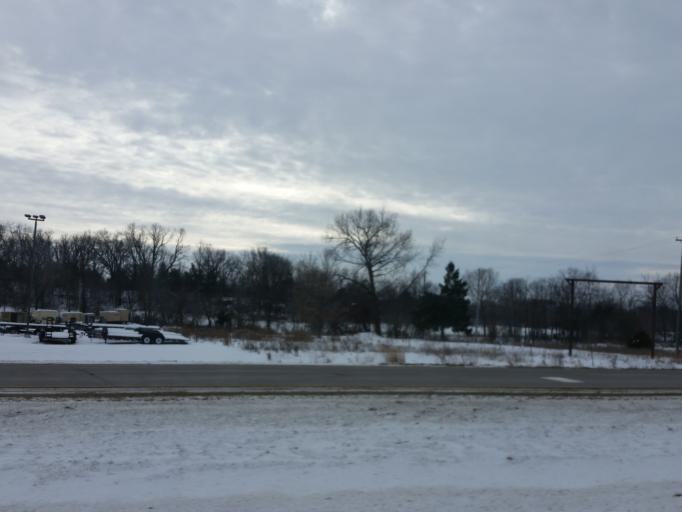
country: US
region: Iowa
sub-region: Dubuque County
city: Dyersville
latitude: 42.4693
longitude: -91.1035
